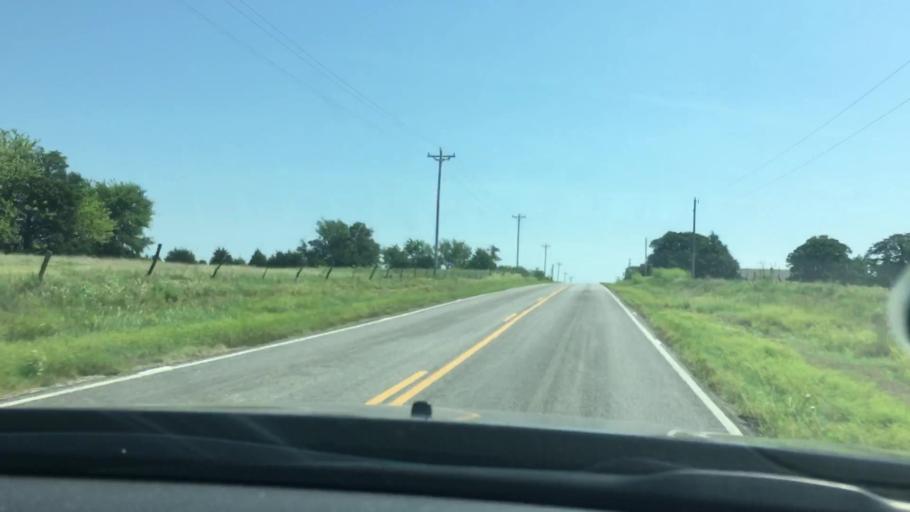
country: US
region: Oklahoma
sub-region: Johnston County
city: Tishomingo
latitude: 34.2741
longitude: -96.5189
